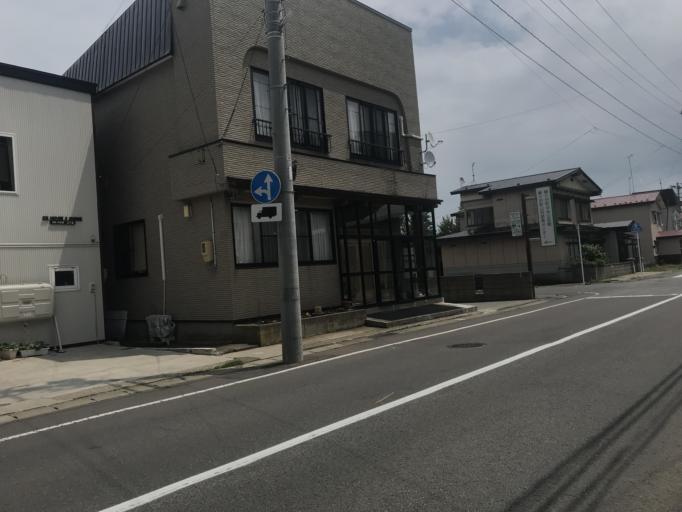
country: JP
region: Aomori
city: Shimokizukuri
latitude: 40.7792
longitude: 140.2083
